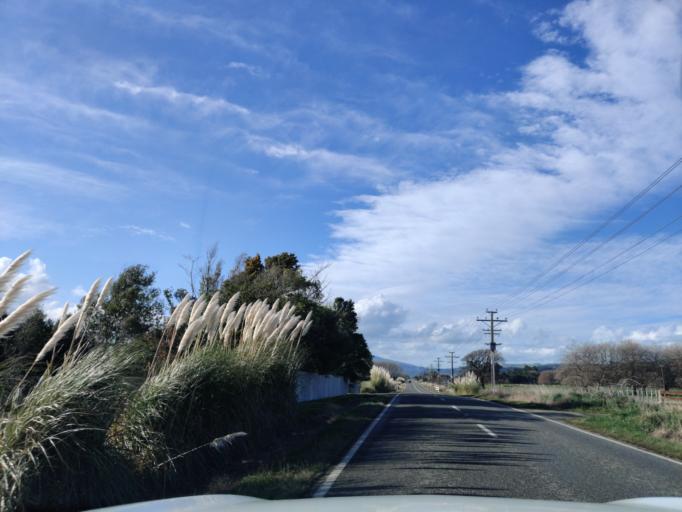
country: NZ
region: Manawatu-Wanganui
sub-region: Palmerston North City
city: Palmerston North
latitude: -40.3571
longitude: 175.6851
